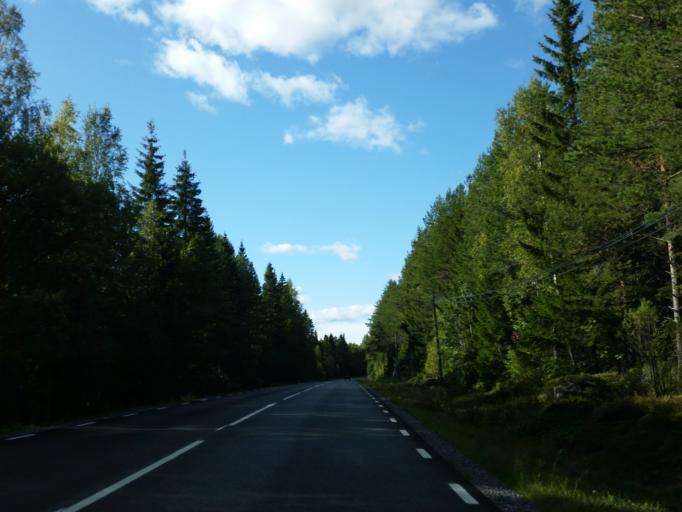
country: SE
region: Vaesterbotten
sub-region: Robertsfors Kommun
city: Robertsfors
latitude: 64.1608
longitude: 20.9399
